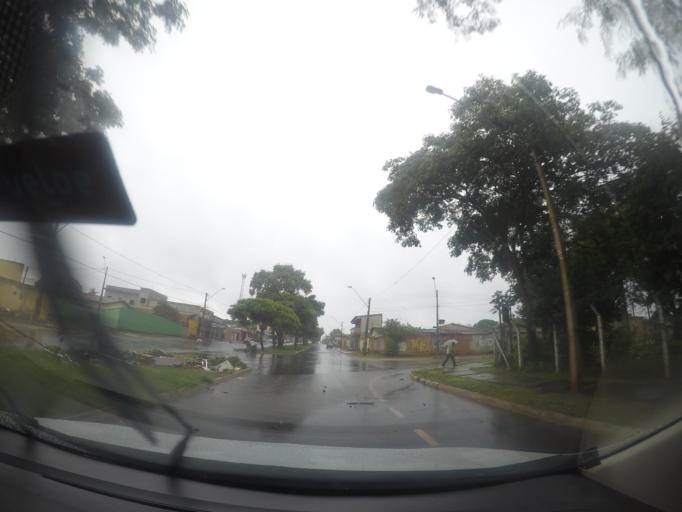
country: BR
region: Goias
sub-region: Goiania
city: Goiania
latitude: -16.5882
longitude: -49.3330
